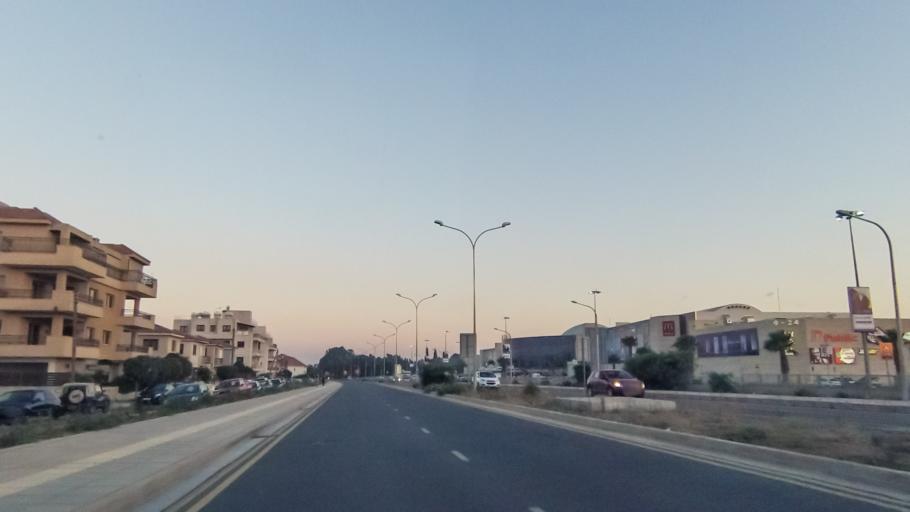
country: CY
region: Limassol
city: Ypsonas
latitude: 34.6554
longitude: 32.9975
